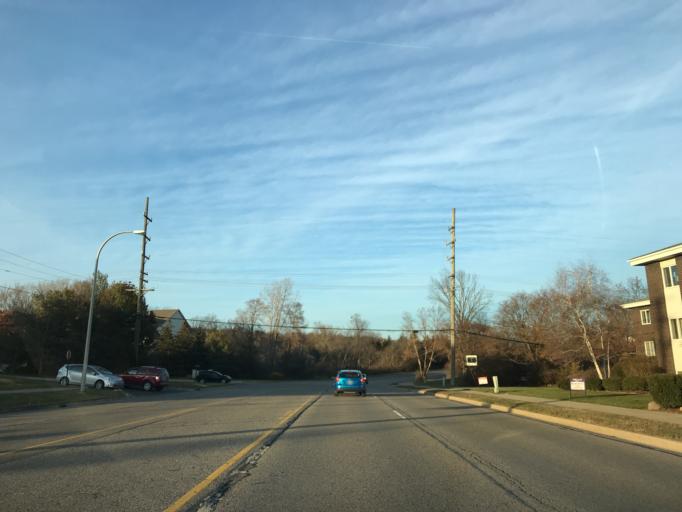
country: US
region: Michigan
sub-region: Washtenaw County
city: Ann Arbor
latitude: 42.2579
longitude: -83.6955
